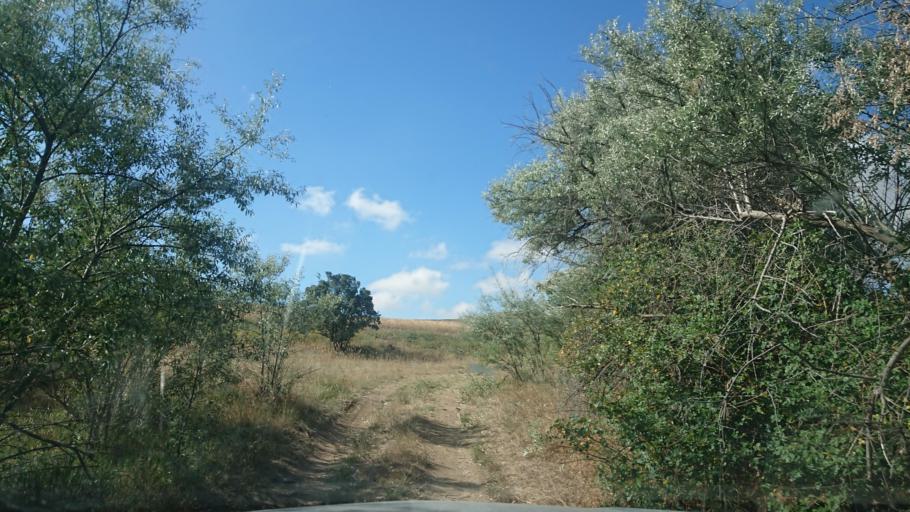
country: TR
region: Aksaray
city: Agacoren
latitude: 38.8467
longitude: 33.9306
